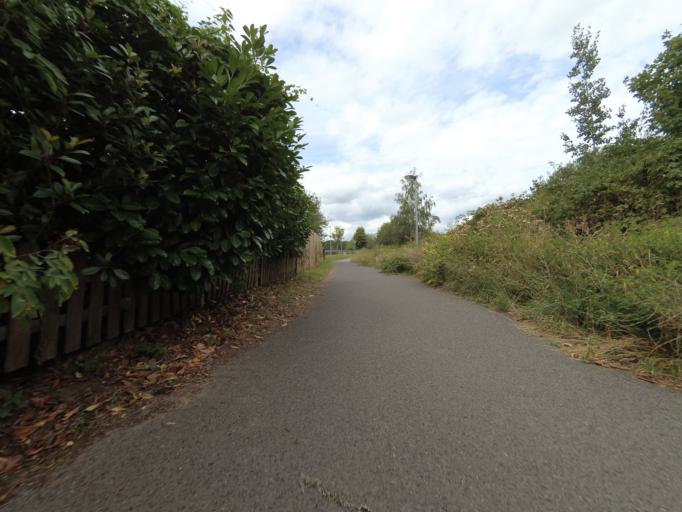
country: DE
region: North Rhine-Westphalia
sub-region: Regierungsbezirk Munster
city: Ahaus
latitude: 52.0906
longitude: 7.0147
